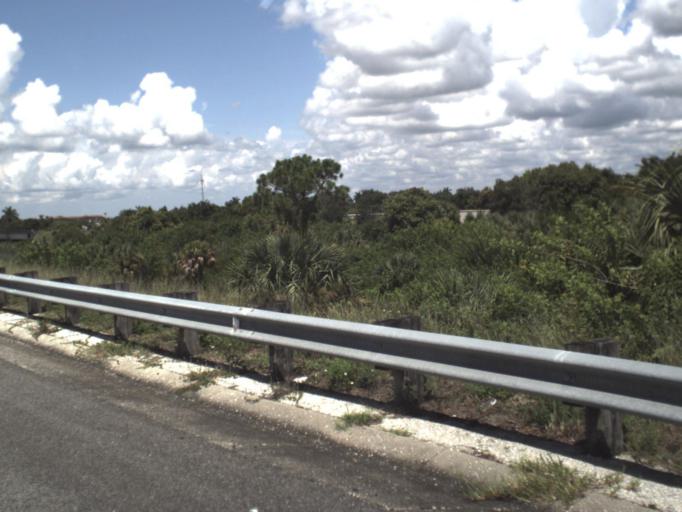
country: US
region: Florida
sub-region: Charlotte County
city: Punta Gorda
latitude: 26.9390
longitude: -82.0254
